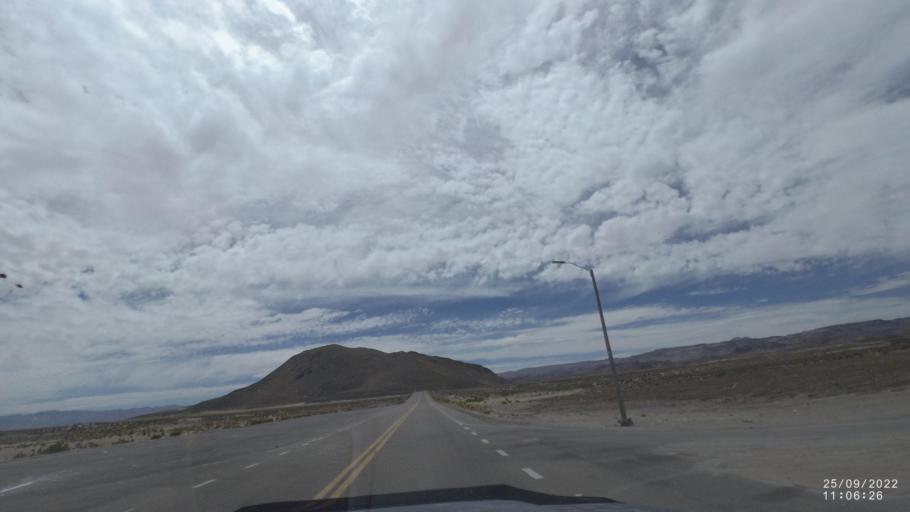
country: BO
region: Oruro
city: Challapata
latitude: -19.3567
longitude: -66.8634
